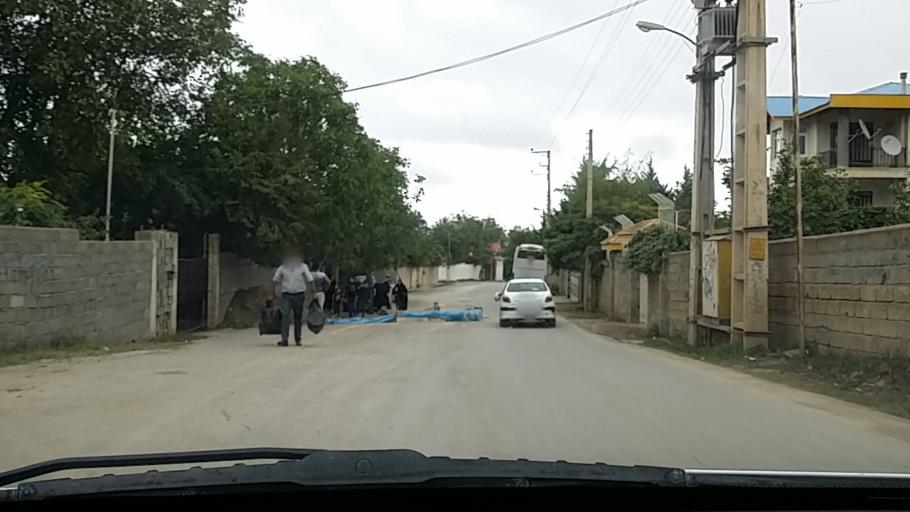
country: IR
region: Mazandaran
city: `Abbasabad
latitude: 36.5013
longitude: 51.1586
